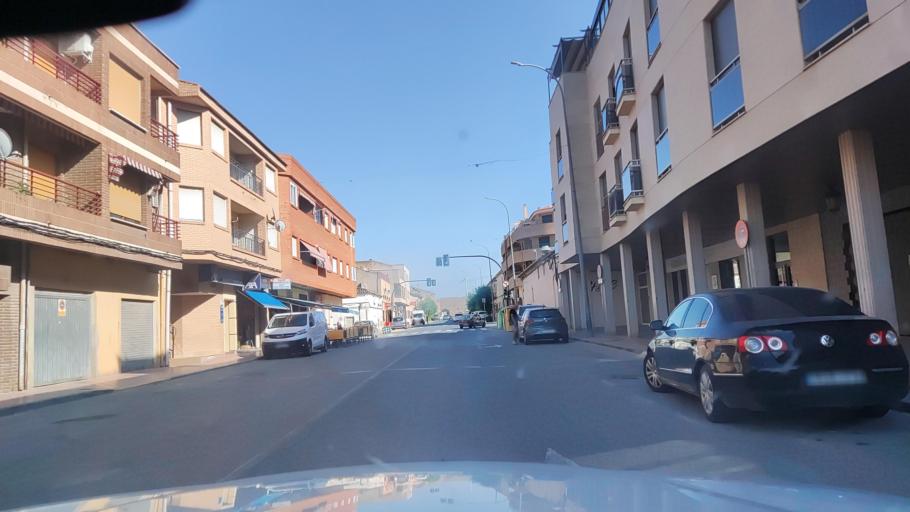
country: ES
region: Castille-La Mancha
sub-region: Provincia de Albacete
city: Pozo-Canada
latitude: 38.8036
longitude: -1.7325
